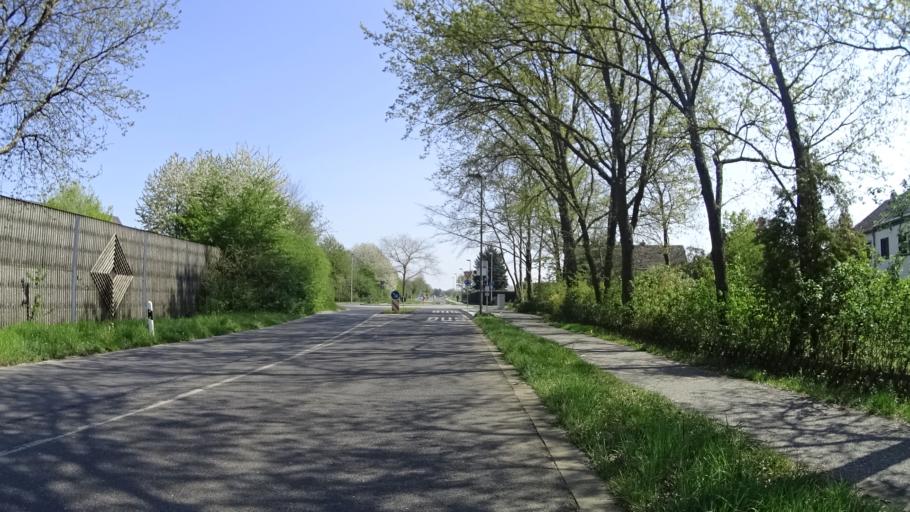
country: DE
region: North Rhine-Westphalia
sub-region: Regierungsbezirk Dusseldorf
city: Meerbusch
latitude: 51.3025
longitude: 6.6905
